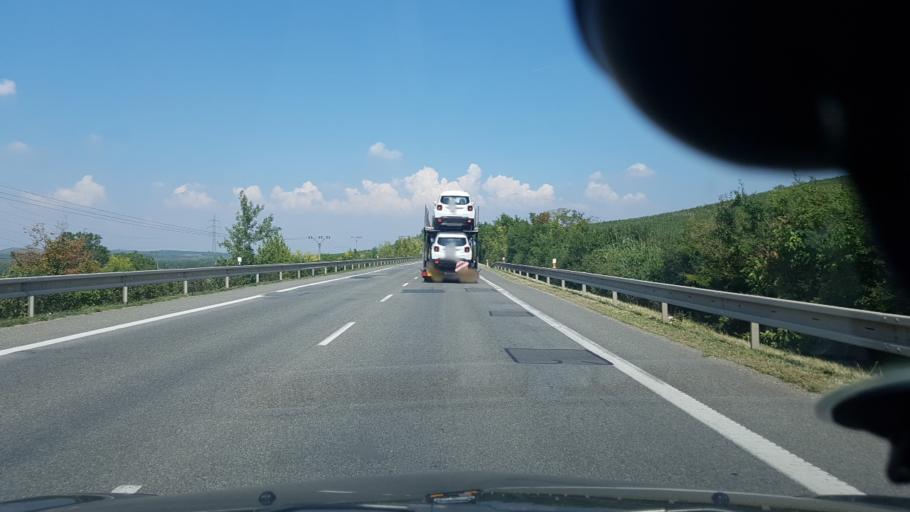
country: CZ
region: South Moravian
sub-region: Okres Breclav
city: Mikulov
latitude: 48.8220
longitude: 16.6173
